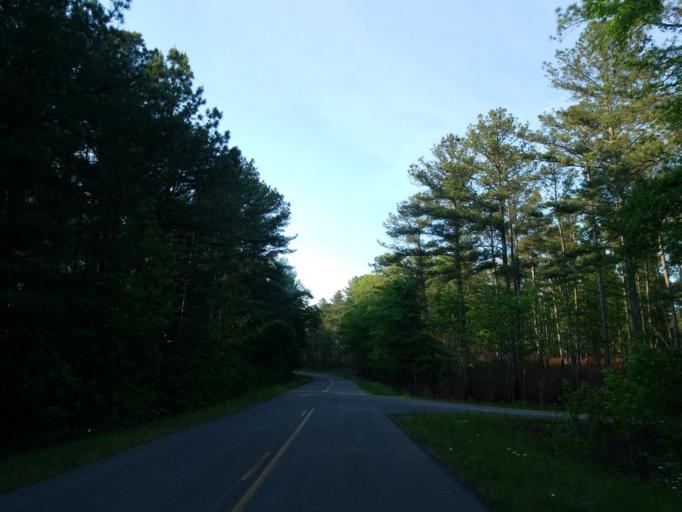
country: US
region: Georgia
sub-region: Gordon County
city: Calhoun
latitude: 34.6070
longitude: -85.0811
